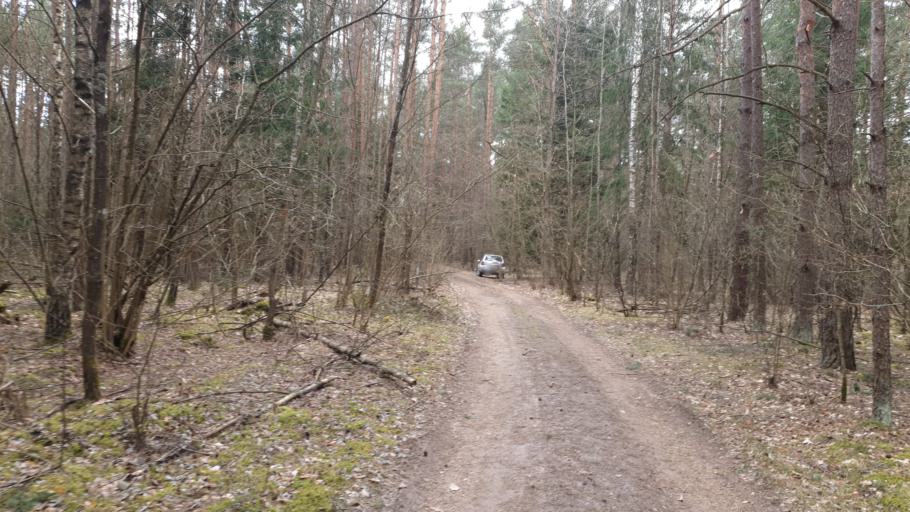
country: LT
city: Grigiskes
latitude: 54.7286
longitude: 25.0349
